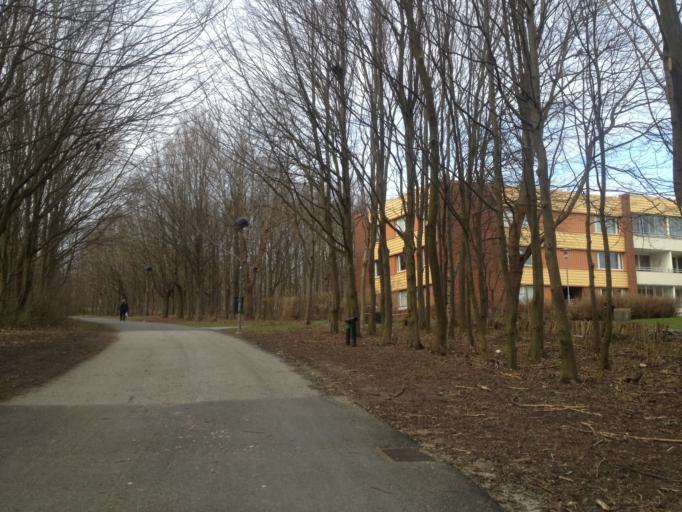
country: SE
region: Skane
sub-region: Lunds Kommun
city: Lund
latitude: 55.6957
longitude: 13.2438
